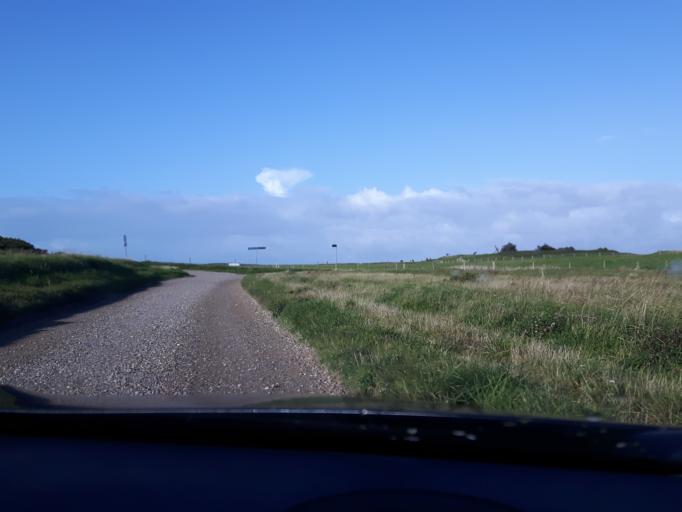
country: DK
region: North Denmark
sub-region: Hjorring Kommune
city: Hjorring
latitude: 57.4625
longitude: 9.7897
